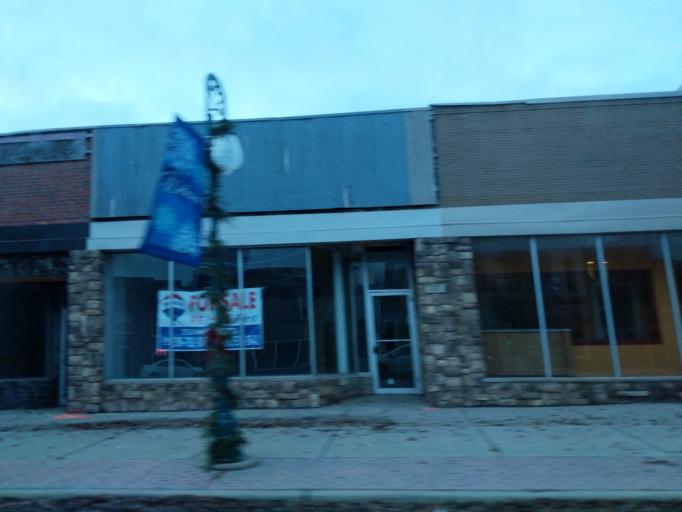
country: US
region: Michigan
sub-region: Lapeer County
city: Almont
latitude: 42.9202
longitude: -83.0452
